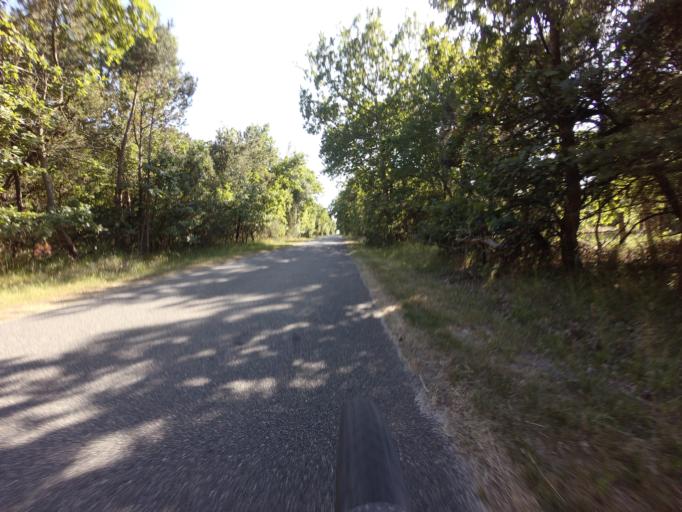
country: DK
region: North Denmark
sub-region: Laeso Kommune
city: Byrum
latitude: 57.2668
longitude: 10.8964
